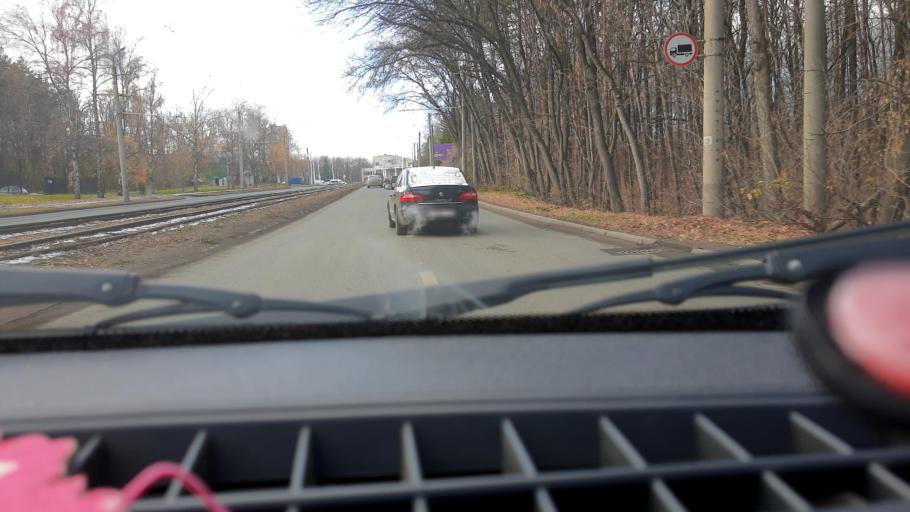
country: RU
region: Bashkortostan
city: Ufa
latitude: 54.7965
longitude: 56.0442
